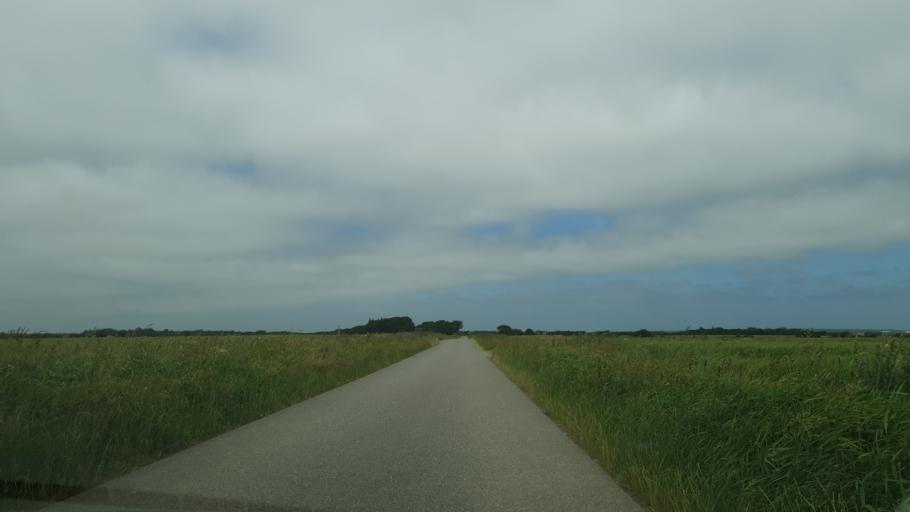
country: DK
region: Central Jutland
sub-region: Ringkobing-Skjern Kommune
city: Skjern
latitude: 55.9287
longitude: 8.4028
